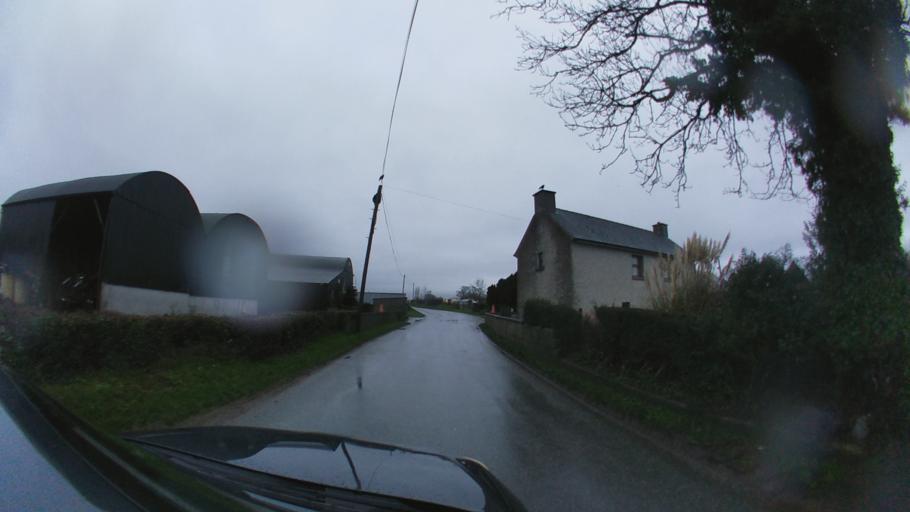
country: IE
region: Leinster
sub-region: County Carlow
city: Bagenalstown
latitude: 52.6458
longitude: -6.9897
